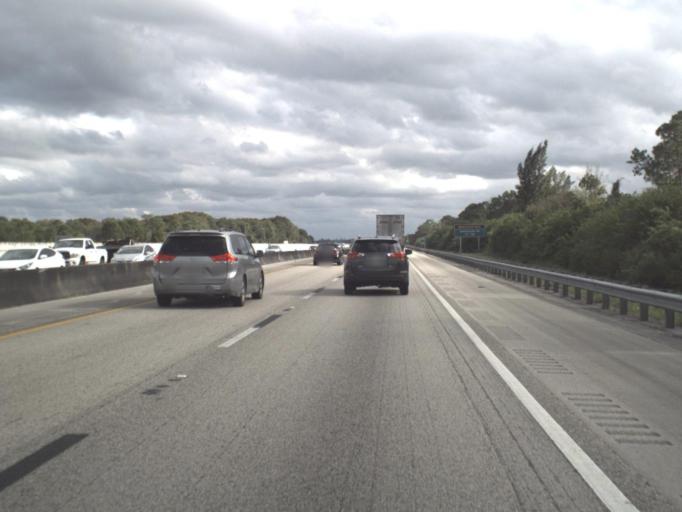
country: US
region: Florida
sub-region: Palm Beach County
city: Limestone Creek
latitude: 26.9605
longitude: -80.1701
